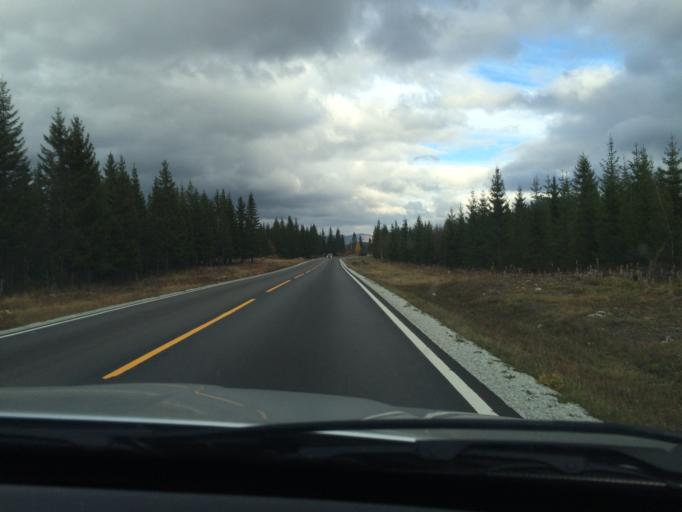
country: NO
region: Nord-Trondelag
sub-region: Namsskogan
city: Namsskogan
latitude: 64.7743
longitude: 12.8794
